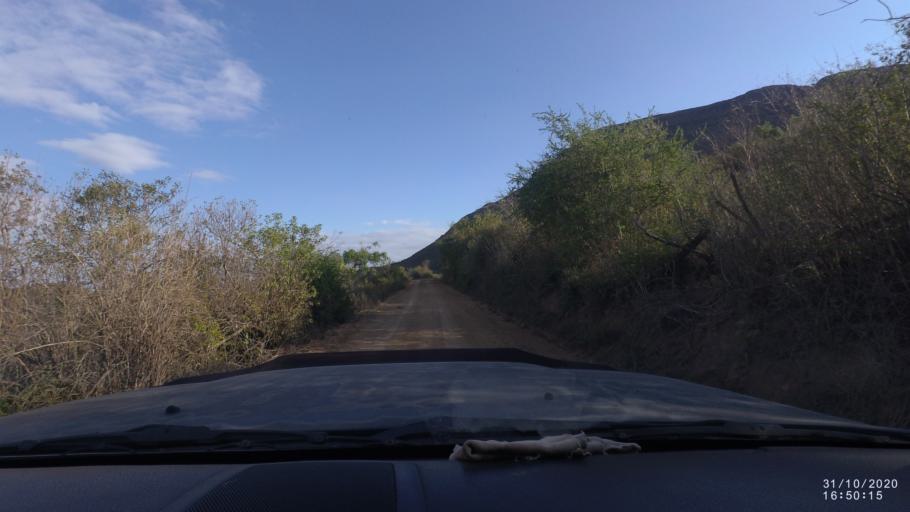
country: BO
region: Chuquisaca
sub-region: Provincia Zudanez
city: Mojocoya
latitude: -18.5078
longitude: -64.5707
